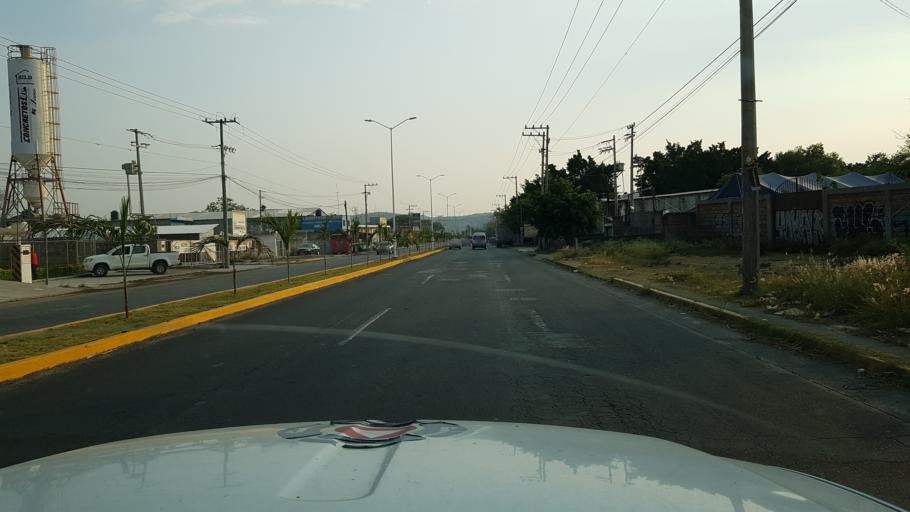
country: MX
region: Morelos
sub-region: Ayala
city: San Pedro Apatlaco
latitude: 18.7968
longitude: -98.9708
